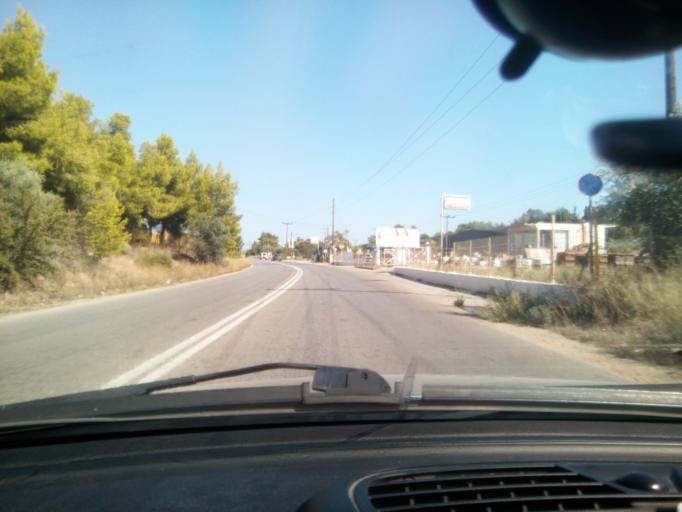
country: GR
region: Central Greece
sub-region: Nomos Evvoias
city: Vasilikon
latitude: 38.4163
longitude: 23.6959
